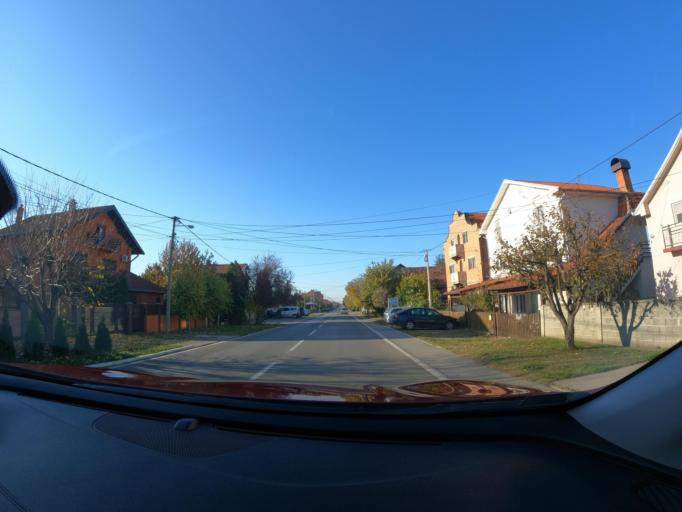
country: RS
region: Central Serbia
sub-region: Belgrade
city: Zemun
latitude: 44.8469
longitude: 20.3436
